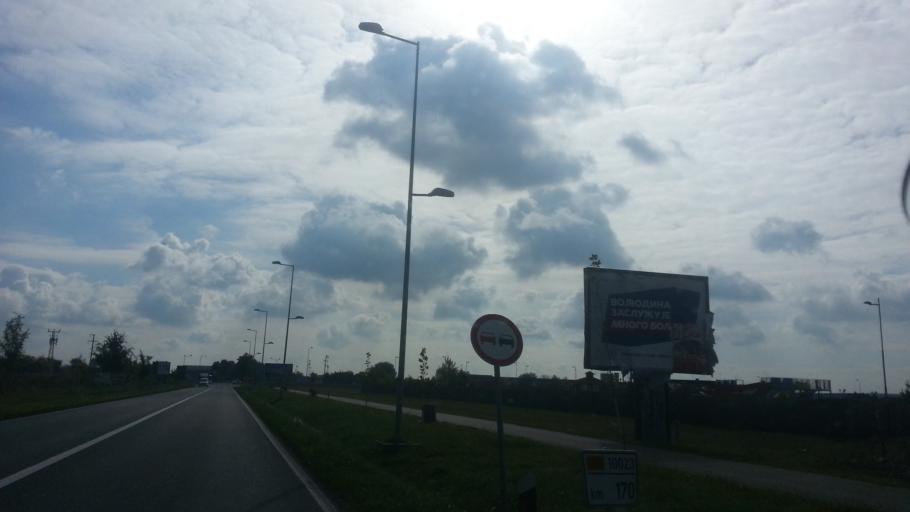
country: RS
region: Autonomna Pokrajina Vojvodina
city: Nova Pazova
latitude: 44.9586
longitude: 20.1975
